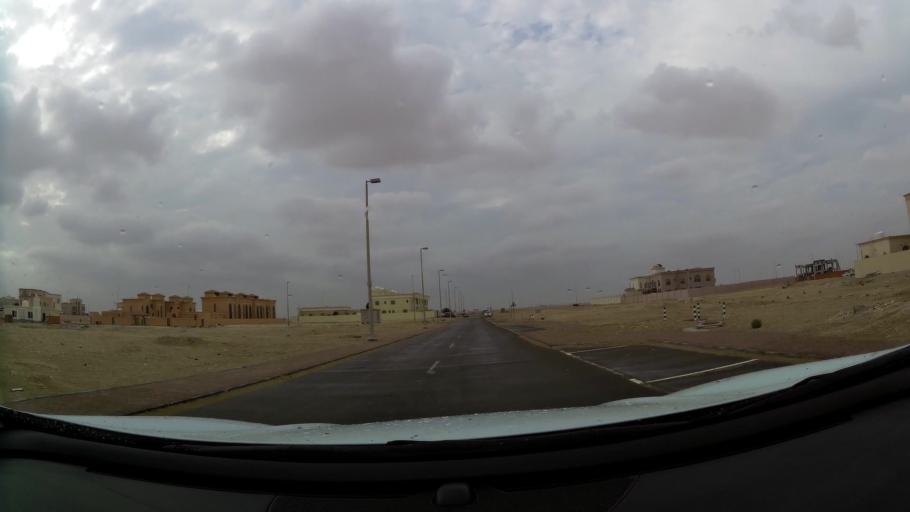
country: AE
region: Abu Dhabi
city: Abu Dhabi
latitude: 24.3598
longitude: 54.6189
